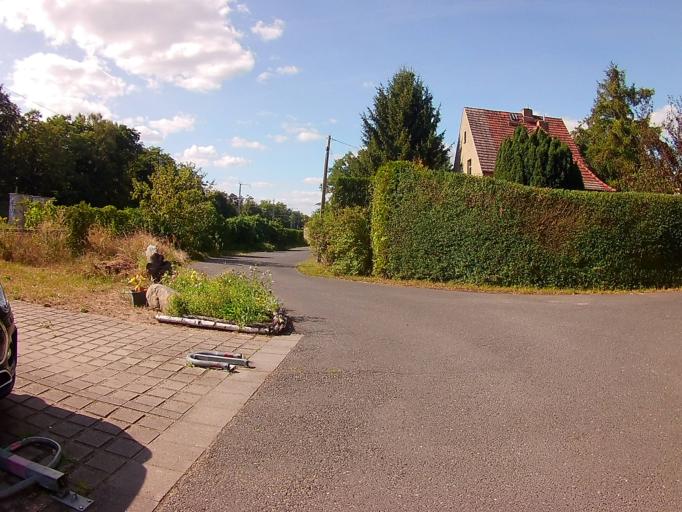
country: DE
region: Brandenburg
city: Zeuthen
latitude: 52.3448
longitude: 13.6304
